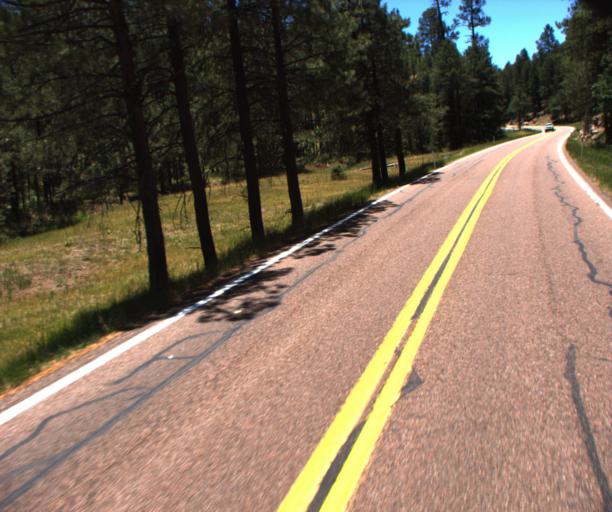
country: US
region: Arizona
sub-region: Gila County
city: Pine
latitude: 34.4998
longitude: -111.3671
